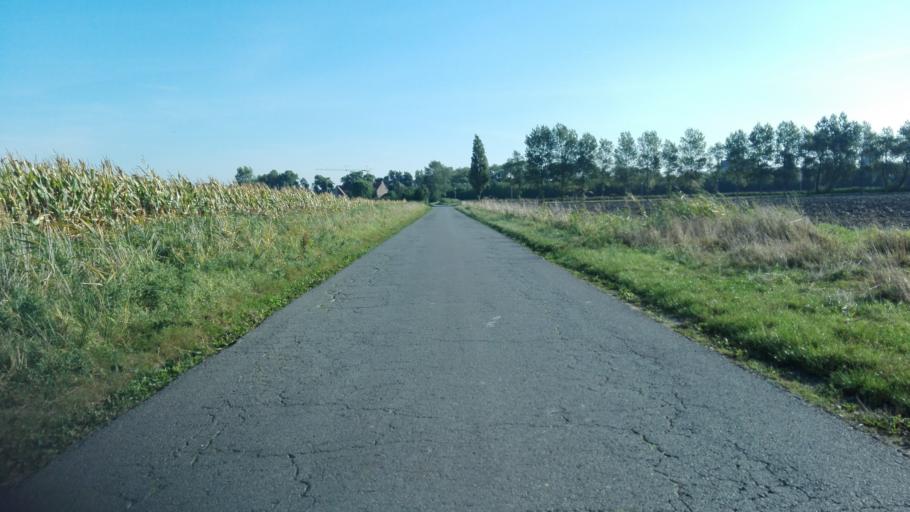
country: BE
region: Flanders
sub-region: Provincie West-Vlaanderen
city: Veurne
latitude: 51.0717
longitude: 2.6500
